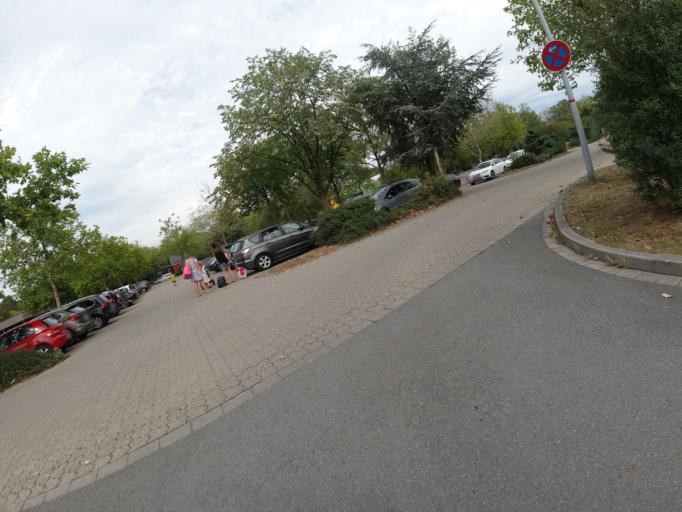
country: DE
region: North Rhine-Westphalia
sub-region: Regierungsbezirk Dusseldorf
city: Moers
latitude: 51.4391
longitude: 6.6176
